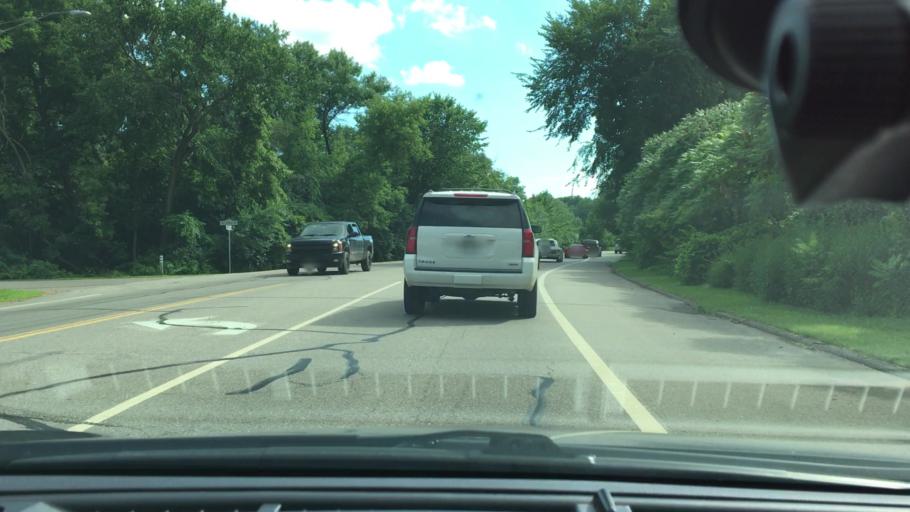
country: US
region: Minnesota
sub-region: Hennepin County
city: Tonka Bay
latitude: 44.9371
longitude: -93.6022
